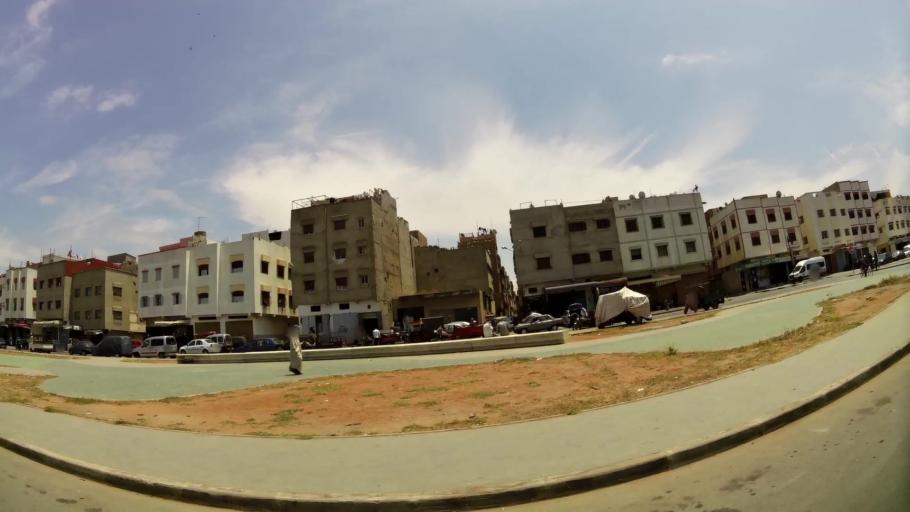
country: MA
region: Rabat-Sale-Zemmour-Zaer
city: Sale
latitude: 34.0674
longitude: -6.7789
